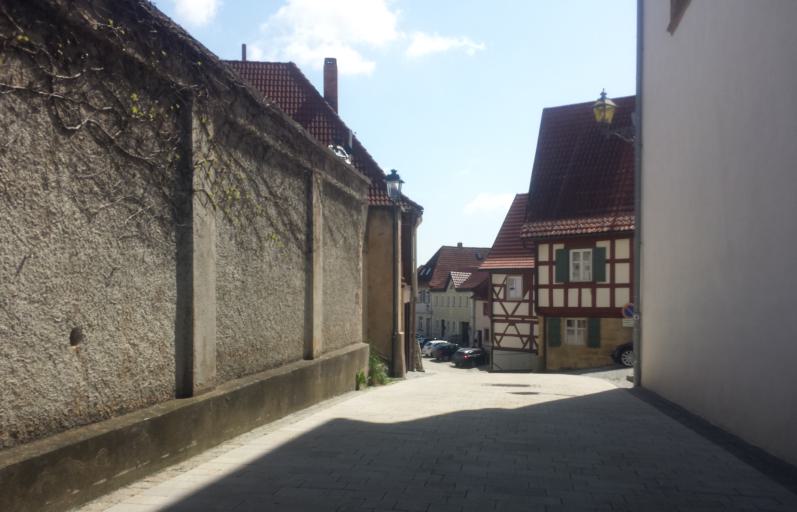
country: DE
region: Bavaria
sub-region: Upper Franconia
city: Burgkunstadt
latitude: 50.1409
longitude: 11.2506
